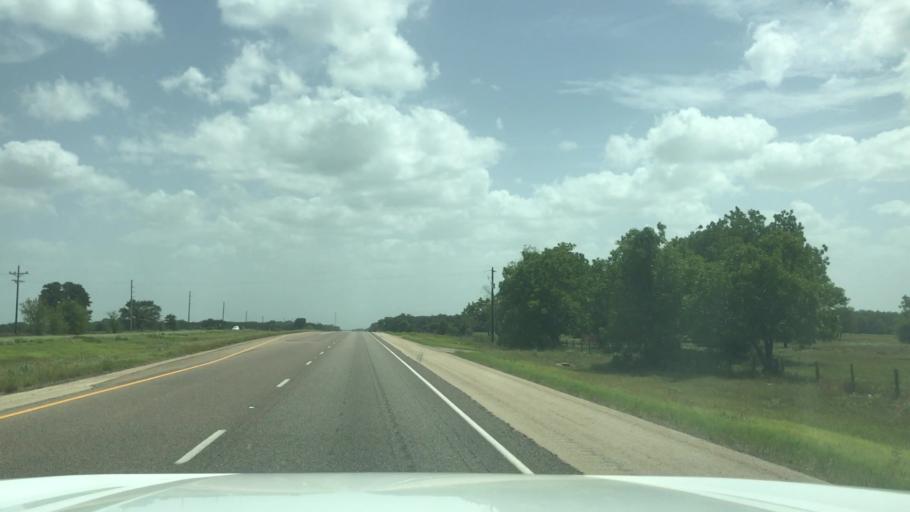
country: US
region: Texas
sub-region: Robertson County
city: Calvert
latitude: 31.0567
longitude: -96.7117
